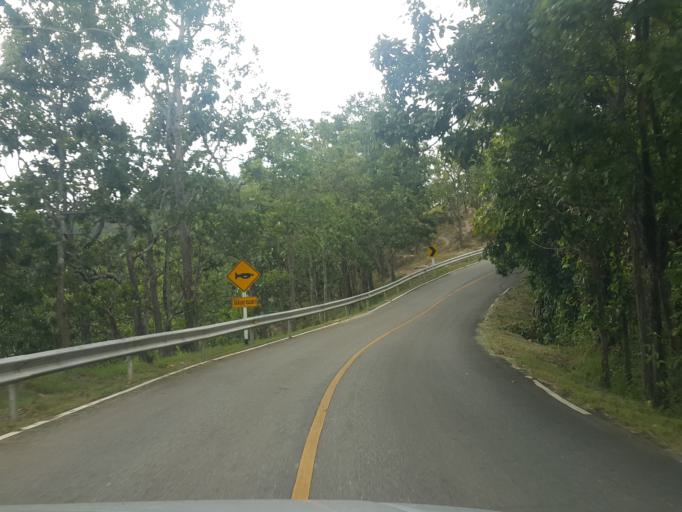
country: TH
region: Chiang Mai
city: Mae Chaem
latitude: 18.5097
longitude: 98.4285
